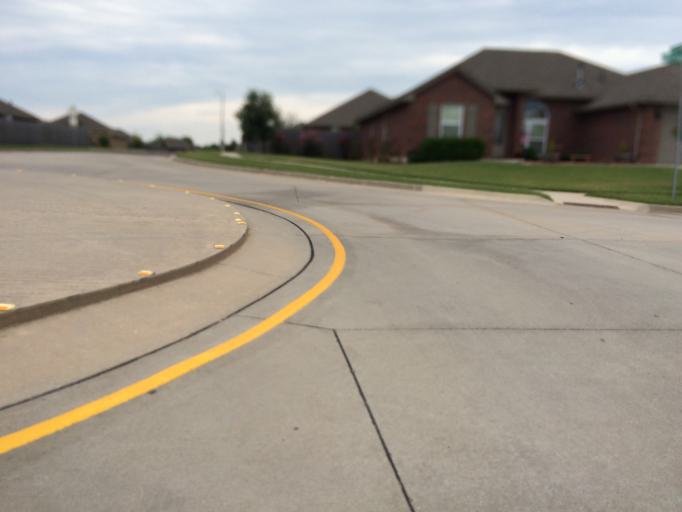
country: US
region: Oklahoma
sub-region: Cleveland County
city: Hall Park
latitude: 35.2454
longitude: -97.4185
